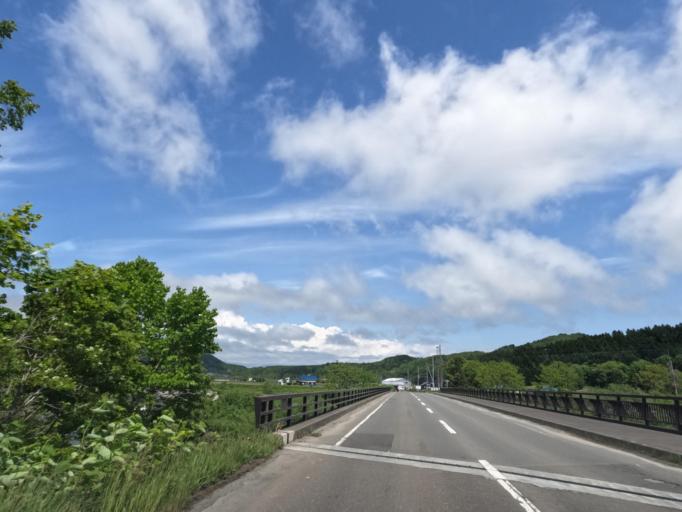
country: JP
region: Hokkaido
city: Tobetsu
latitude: 43.2977
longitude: 141.5446
